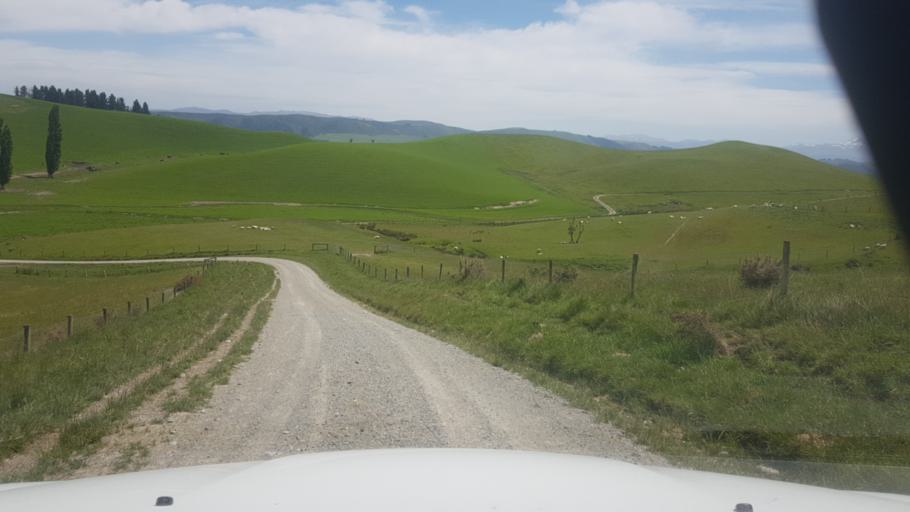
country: NZ
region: Canterbury
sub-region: Timaru District
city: Pleasant Point
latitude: -44.1282
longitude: 171.0121
